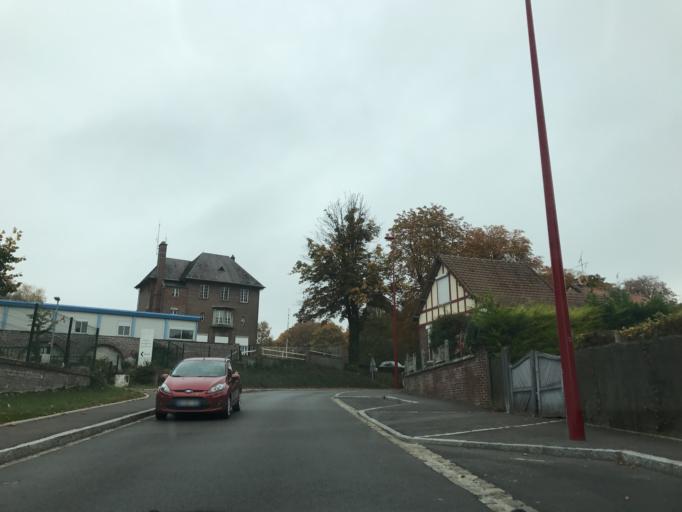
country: FR
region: Picardie
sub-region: Departement de la Somme
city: Peronne
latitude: 49.9337
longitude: 2.9306
